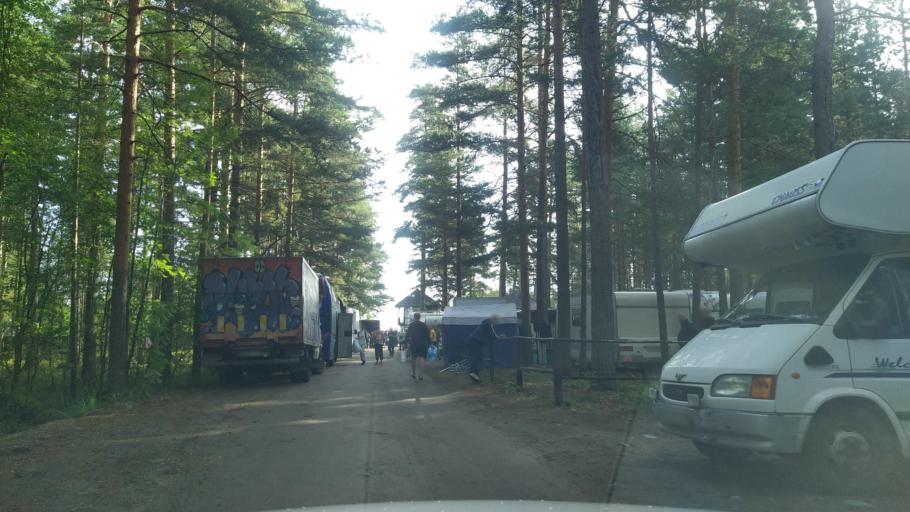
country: RU
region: Leningrad
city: Priozersk
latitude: 60.9730
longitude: 30.3037
